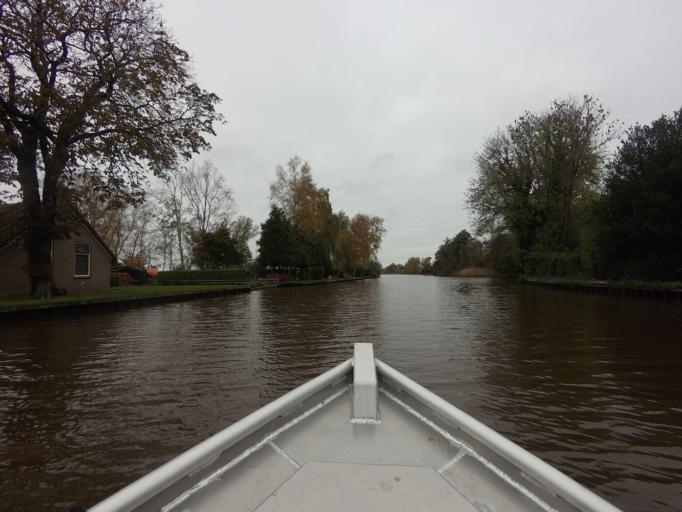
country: NL
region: Overijssel
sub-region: Gemeente Steenwijkerland
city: Blokzijl
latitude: 52.7635
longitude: 5.9920
